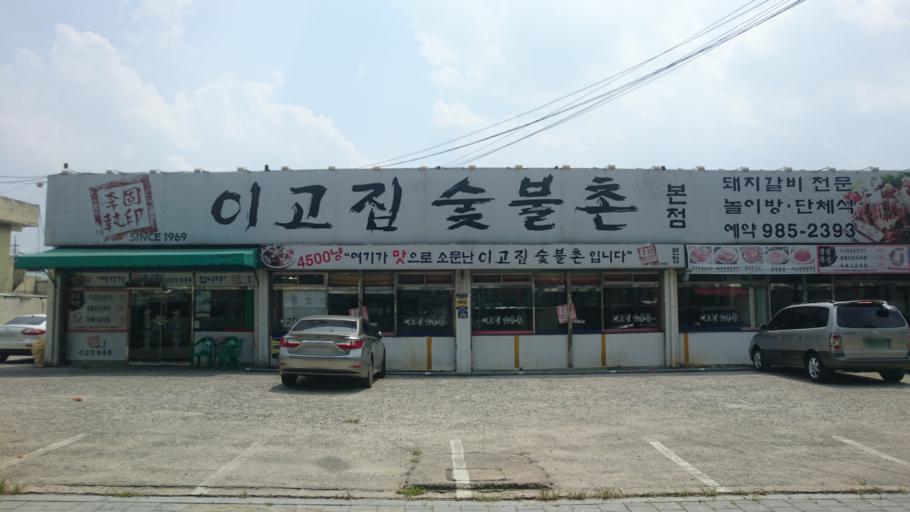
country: KR
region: Gyeongsangbuk-do
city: Gyeongsan-si
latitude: 35.8765
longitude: 128.6804
